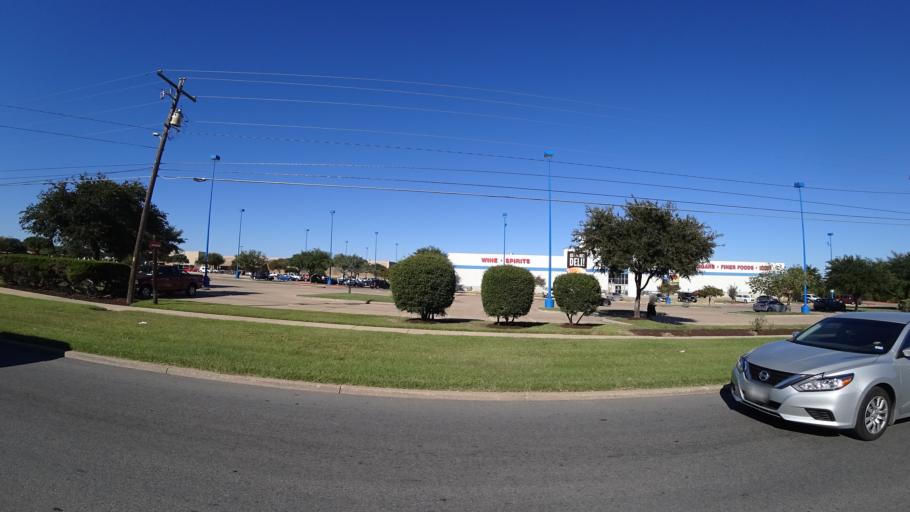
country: US
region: Texas
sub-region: Travis County
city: Rollingwood
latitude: 30.2337
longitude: -97.8193
